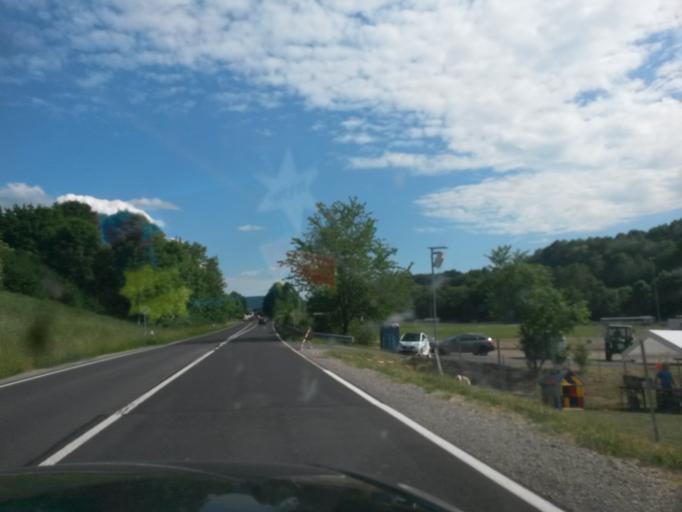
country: DE
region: Hesse
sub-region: Regierungsbezirk Kassel
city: Hilders
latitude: 50.5772
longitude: 9.9963
